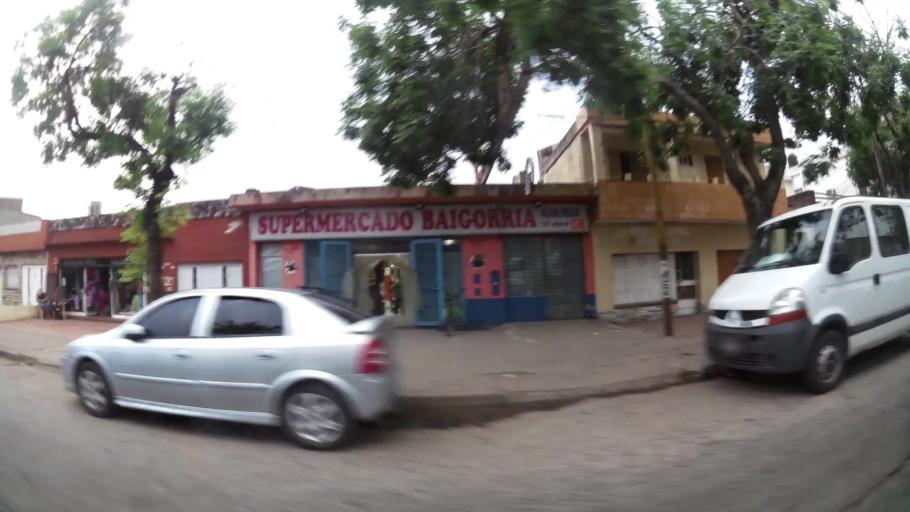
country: AR
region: Santa Fe
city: Granadero Baigorria
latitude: -32.8931
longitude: -60.7006
